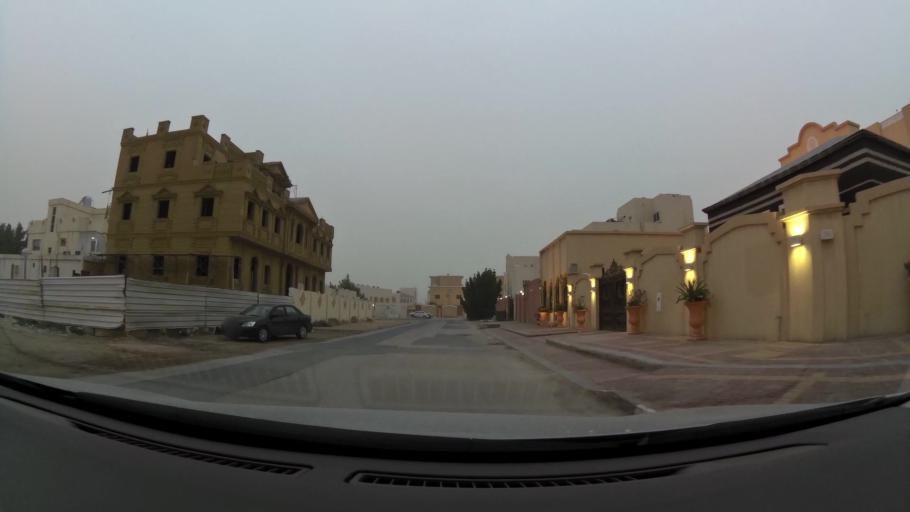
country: QA
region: Baladiyat ad Dawhah
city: Doha
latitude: 25.2355
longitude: 51.4974
